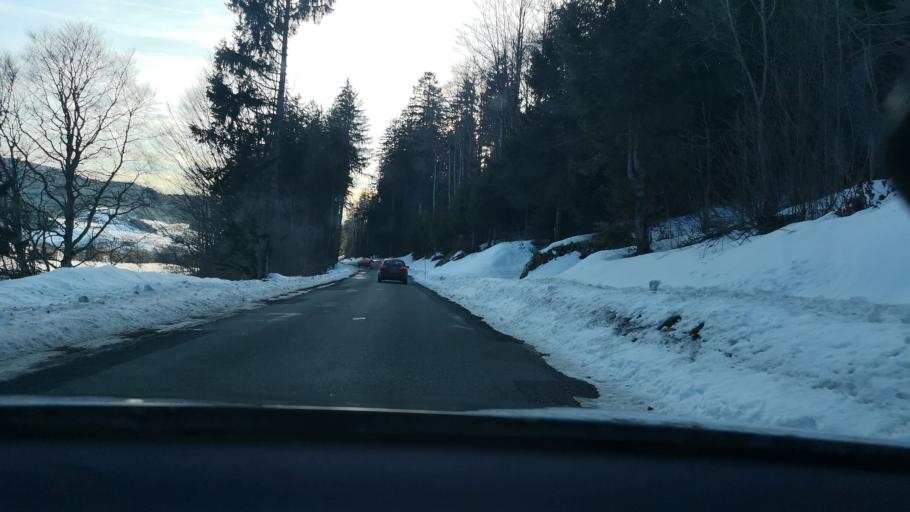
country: FR
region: Franche-Comte
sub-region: Departement du Doubs
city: Gilley
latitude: 46.9568
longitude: 6.4604
